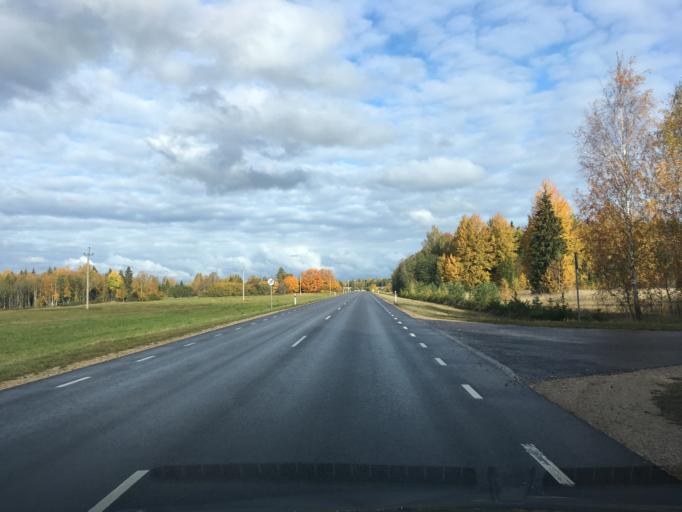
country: EE
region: Harju
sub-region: Raasiku vald
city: Raasiku
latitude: 59.1981
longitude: 25.1843
